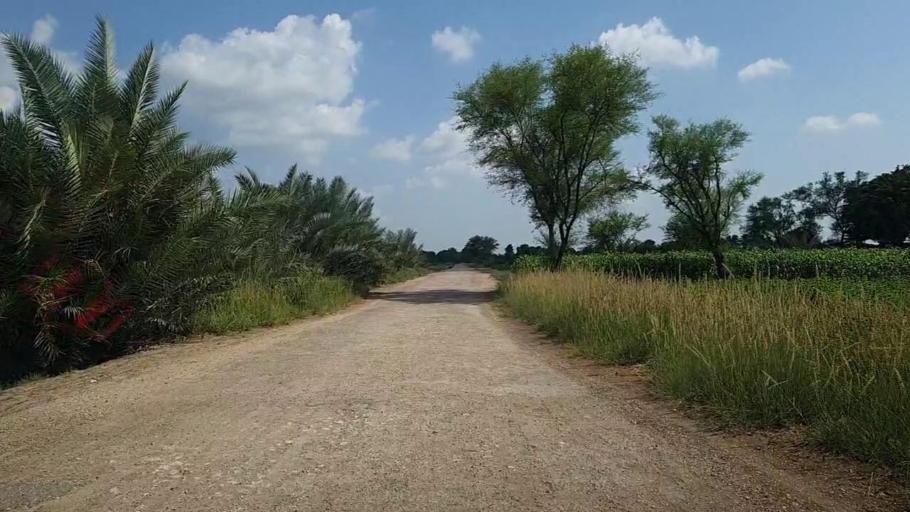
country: PK
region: Sindh
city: Kandiaro
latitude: 26.9956
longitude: 68.3053
